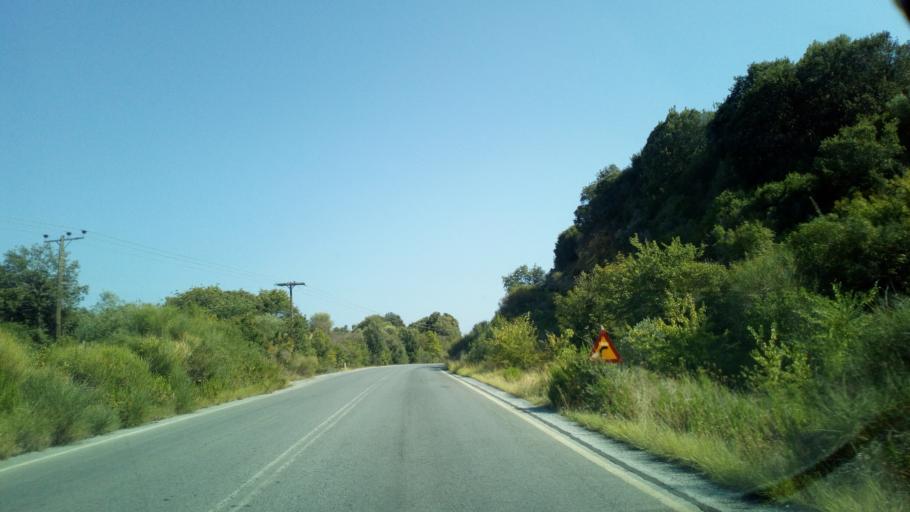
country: GR
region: Central Macedonia
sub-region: Nomos Thessalonikis
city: Stavros
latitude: 40.6411
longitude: 23.7488
